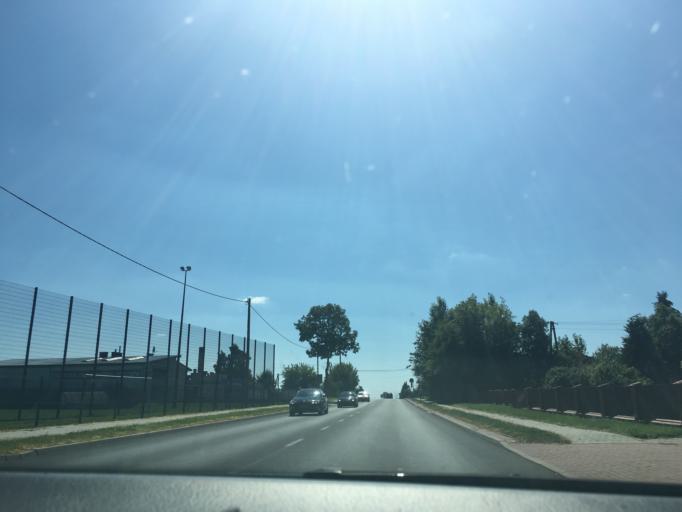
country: PL
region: Lublin Voivodeship
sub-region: Powiat janowski
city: Modliborzyce
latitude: 50.7502
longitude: 22.3355
